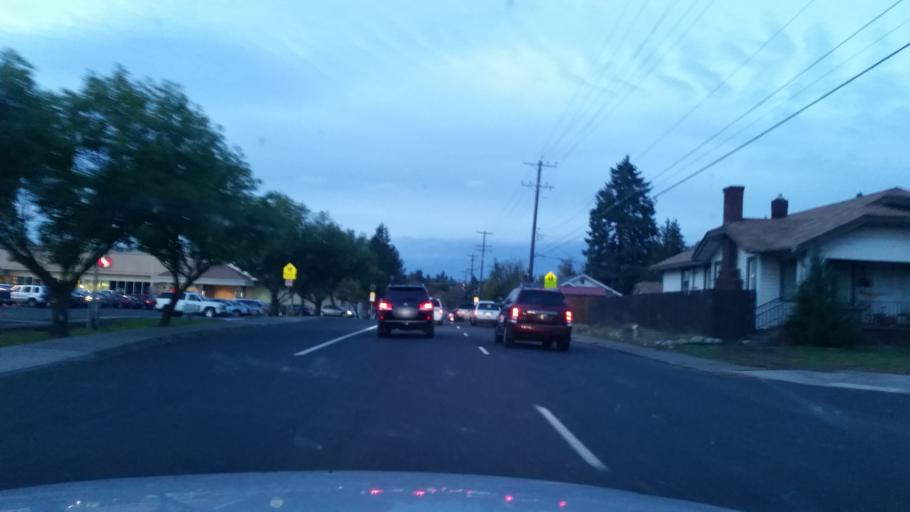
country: US
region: Washington
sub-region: Spokane County
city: Spokane
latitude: 47.6794
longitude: -117.4355
